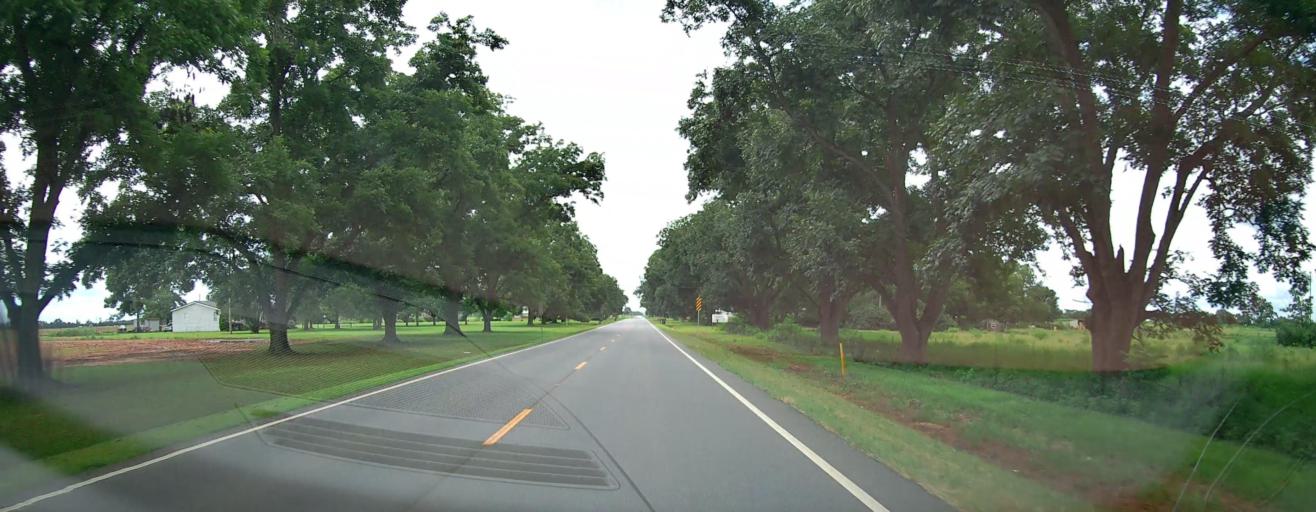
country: US
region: Georgia
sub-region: Macon County
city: Montezuma
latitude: 32.2931
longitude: -83.9669
